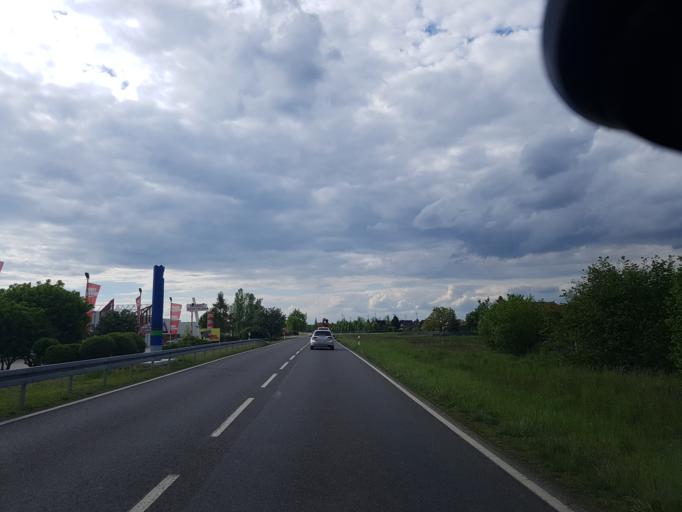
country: DE
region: Brandenburg
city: Grossraschen
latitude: 51.5808
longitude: 14.0296
